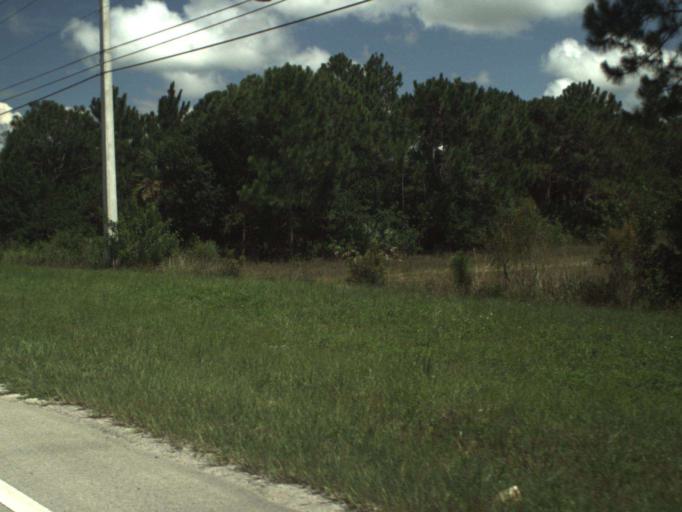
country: US
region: Florida
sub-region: Indian River County
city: Fellsmere
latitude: 27.7671
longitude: -80.5369
